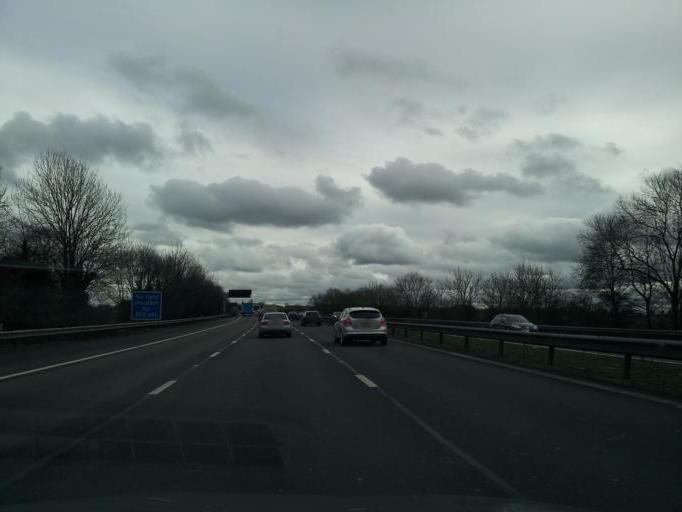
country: GB
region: England
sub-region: Staffordshire
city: Stone
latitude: 52.8957
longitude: -2.1822
